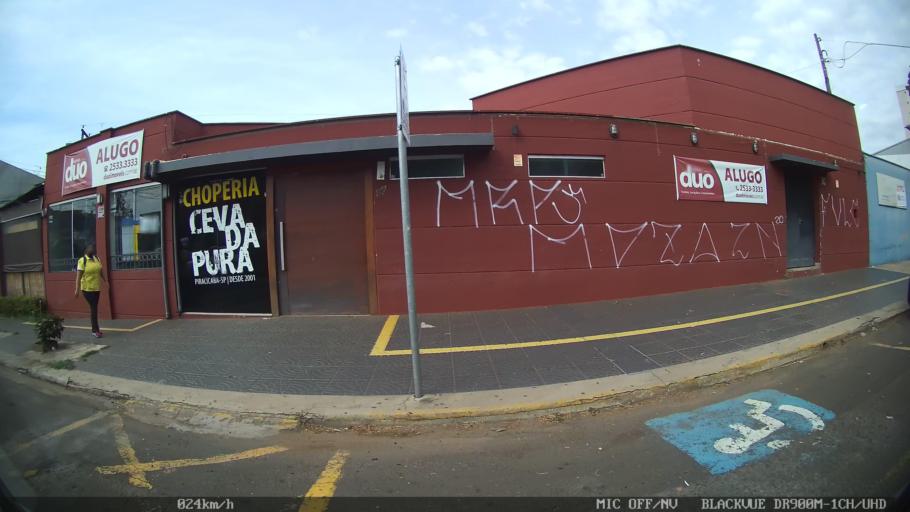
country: BR
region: Sao Paulo
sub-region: Piracicaba
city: Piracicaba
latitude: -22.7102
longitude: -47.6539
